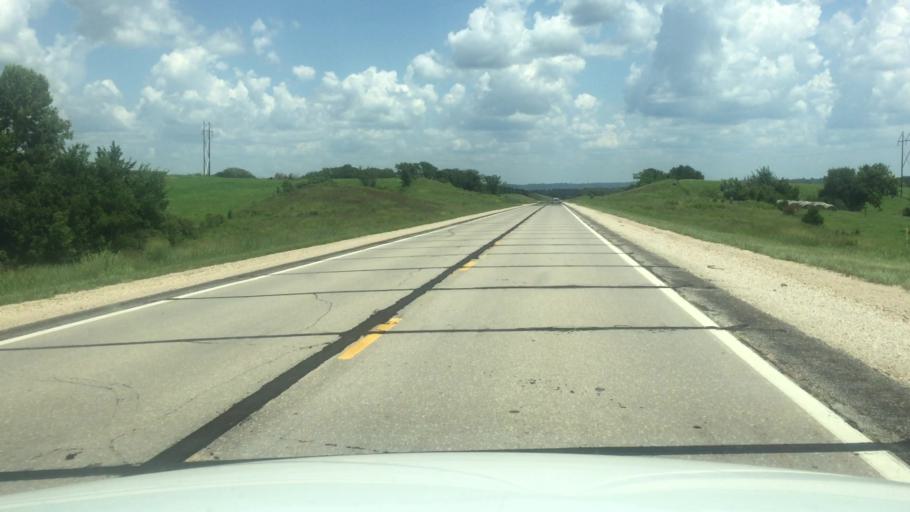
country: US
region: Kansas
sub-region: Atchison County
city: Atchison
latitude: 39.5571
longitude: -95.1795
